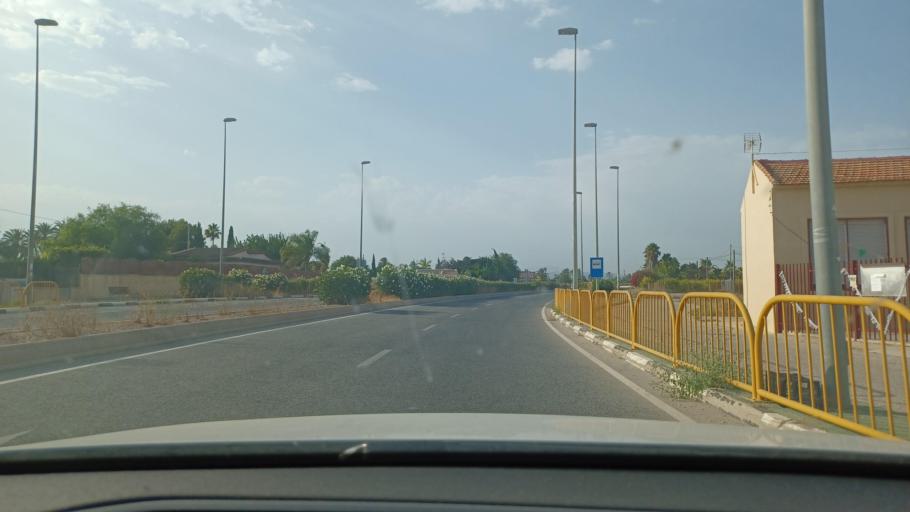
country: ES
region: Valencia
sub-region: Provincia de Alicante
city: Elche
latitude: 38.2149
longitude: -0.6973
